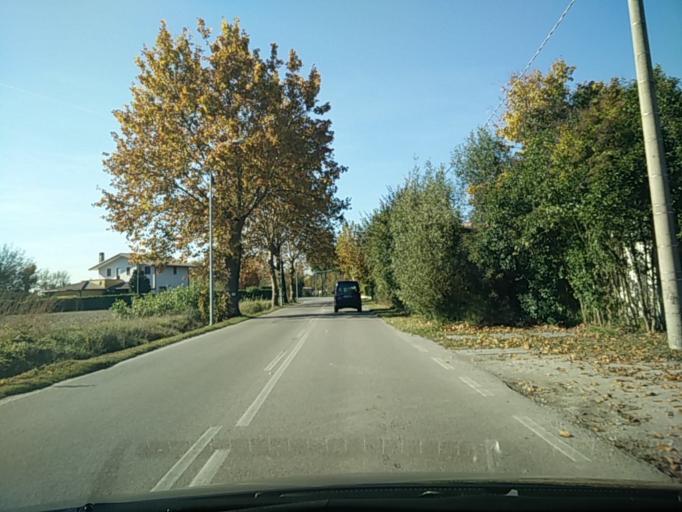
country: IT
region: Veneto
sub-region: Provincia di Treviso
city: Breda
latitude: 45.7169
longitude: 12.3216
